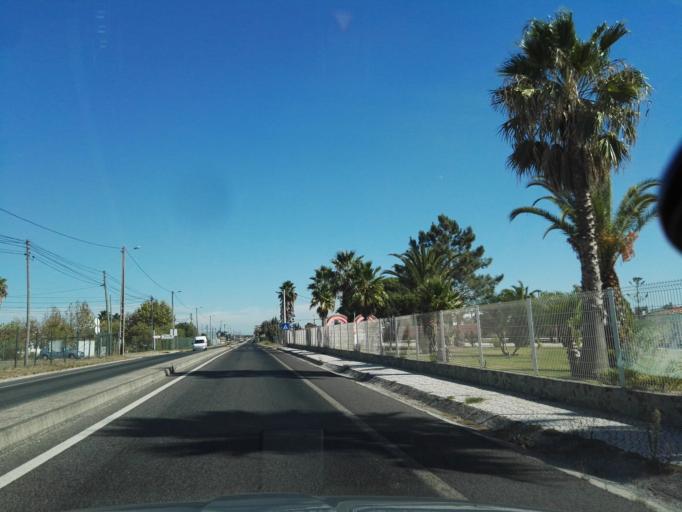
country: PT
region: Santarem
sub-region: Benavente
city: Samora Correia
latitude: 38.9165
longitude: -8.8661
